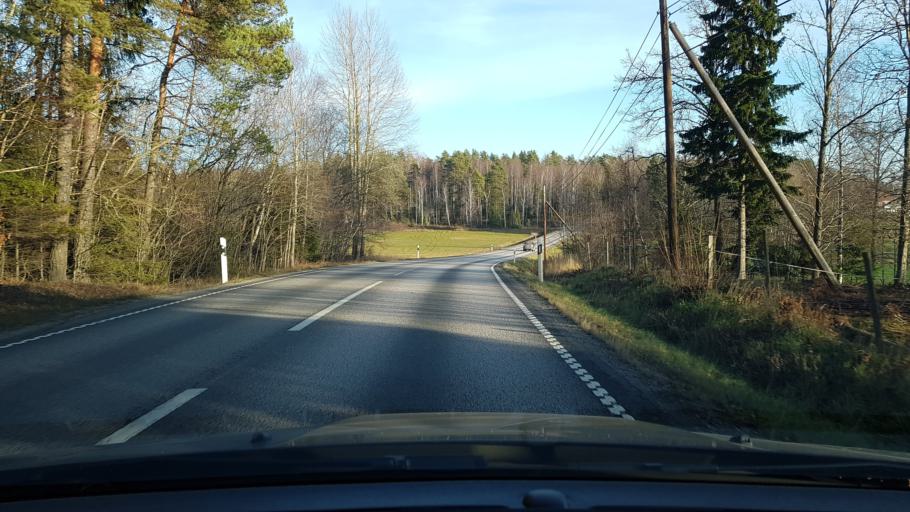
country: SE
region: Stockholm
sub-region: Norrtalje Kommun
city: Nykvarn
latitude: 59.7401
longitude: 18.3048
